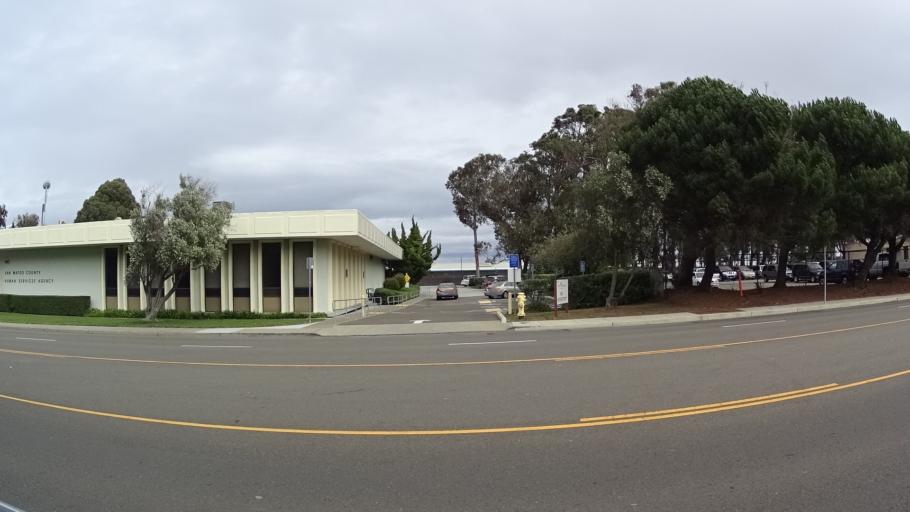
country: US
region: California
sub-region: San Mateo County
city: South San Francisco
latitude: 37.6443
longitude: -122.4219
